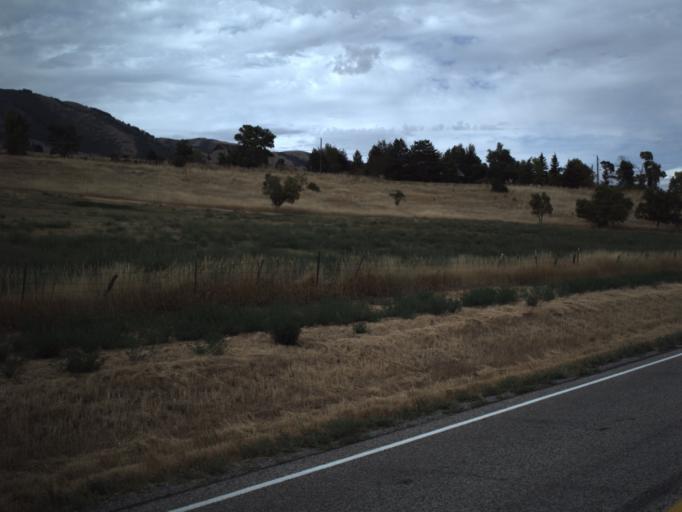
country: US
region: Utah
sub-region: Cache County
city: Mendon
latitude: 41.6977
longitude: -111.9747
